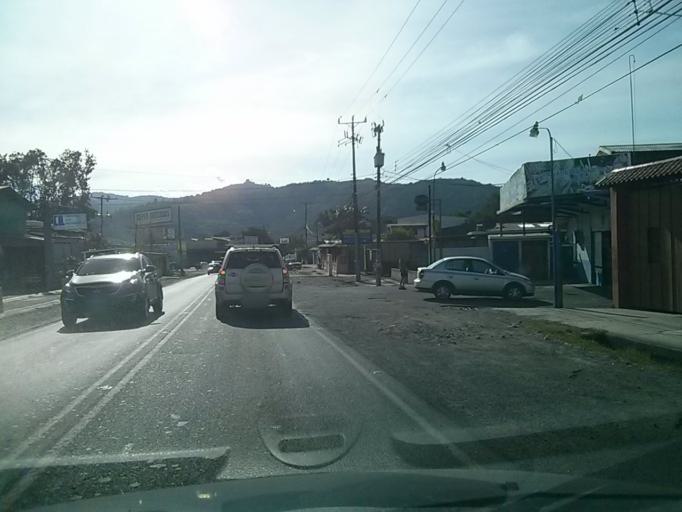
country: CR
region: Cartago
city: Cartago
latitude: 9.8809
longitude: -83.9343
